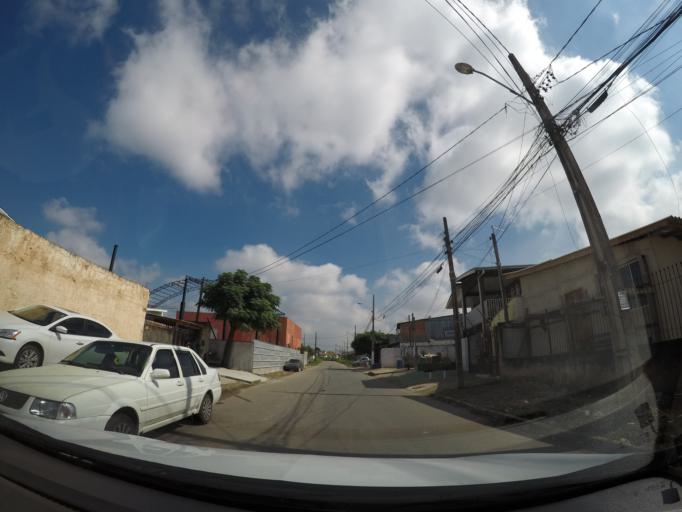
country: BR
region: Parana
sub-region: Sao Jose Dos Pinhais
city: Sao Jose dos Pinhais
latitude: -25.4977
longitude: -49.2207
